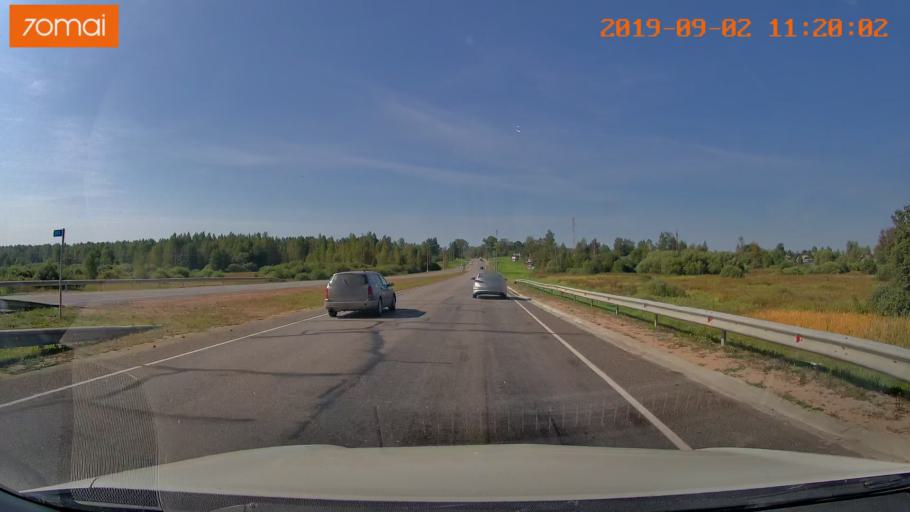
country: RU
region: Smolensk
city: Roslavl'
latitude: 54.0442
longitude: 33.0607
